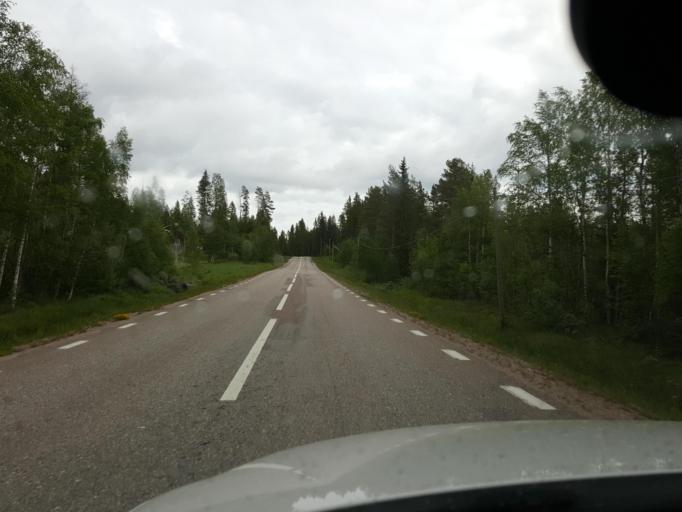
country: SE
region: Gaevleborg
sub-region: Ljusdals Kommun
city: Farila
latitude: 61.7575
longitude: 15.5243
